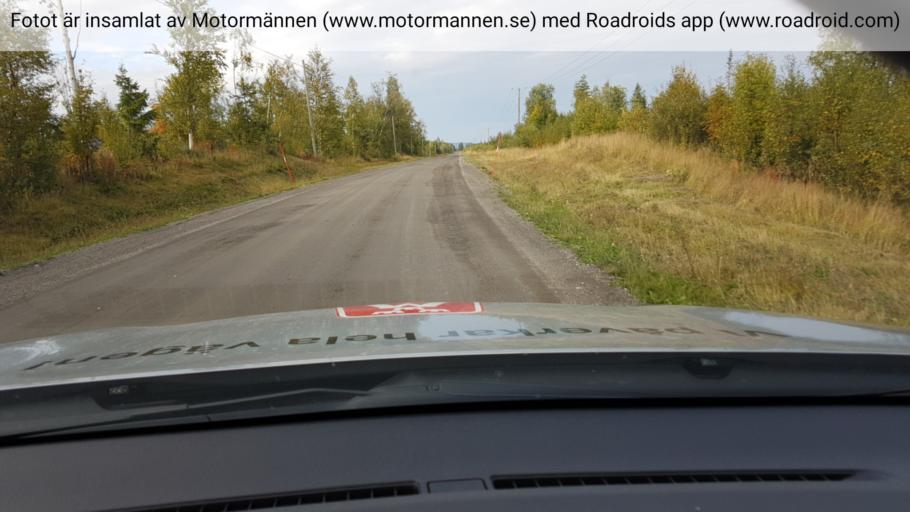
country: SE
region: Jaemtland
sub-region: Stroemsunds Kommun
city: Stroemsund
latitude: 63.9849
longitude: 15.8163
